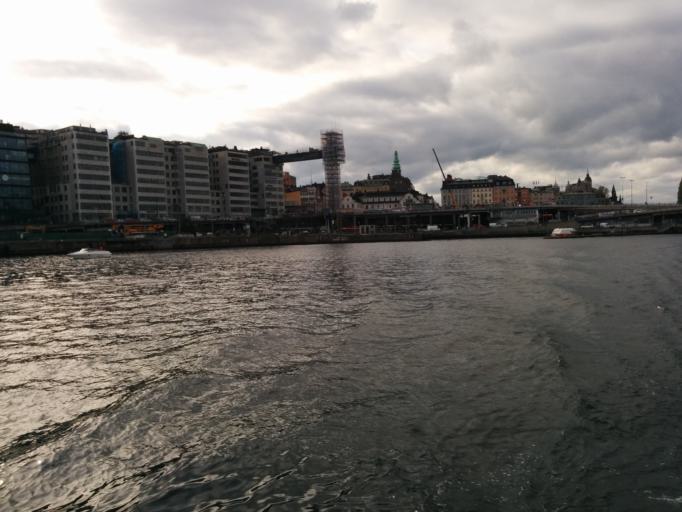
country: SE
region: Stockholm
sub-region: Stockholms Kommun
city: Stockholm
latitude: 59.3210
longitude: 18.0775
